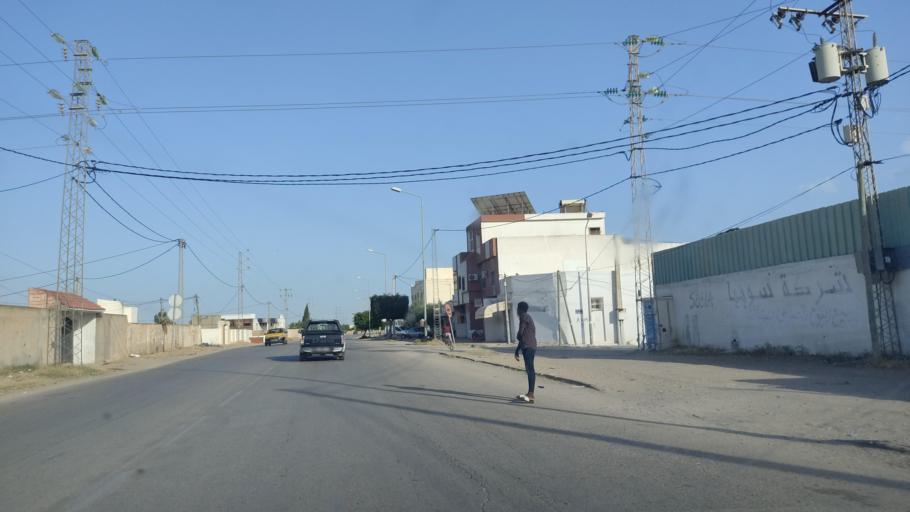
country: TN
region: Safaqis
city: Sfax
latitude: 34.7938
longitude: 10.6837
